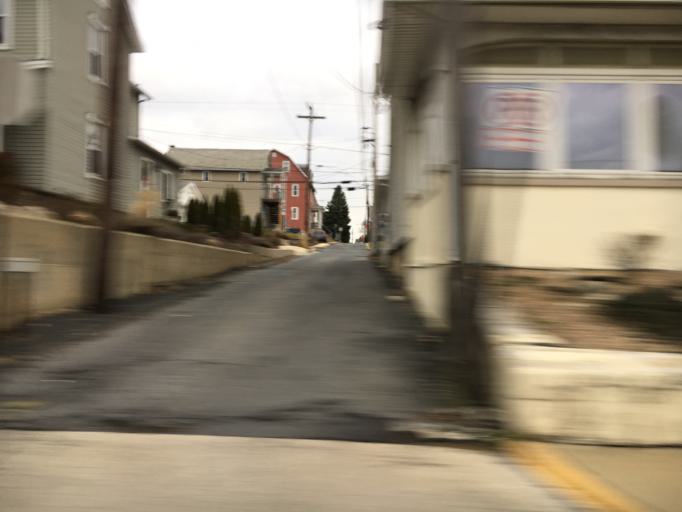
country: US
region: Pennsylvania
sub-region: Northampton County
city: Northampton
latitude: 40.6911
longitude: -75.4994
